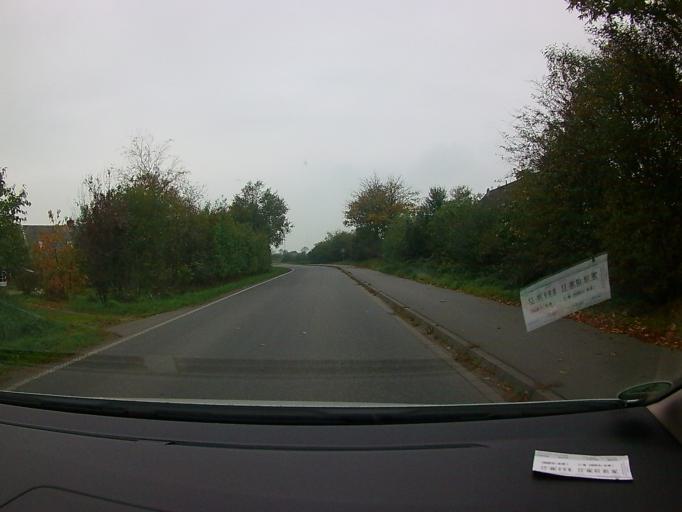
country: DE
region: Schleswig-Holstein
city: Bordelum
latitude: 54.6354
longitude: 8.9201
